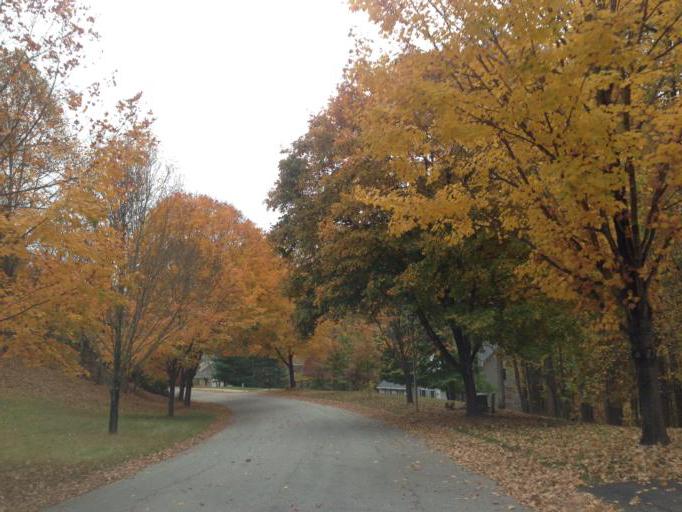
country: US
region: Maryland
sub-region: Howard County
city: Ellicott City
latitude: 39.3123
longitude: -76.8270
